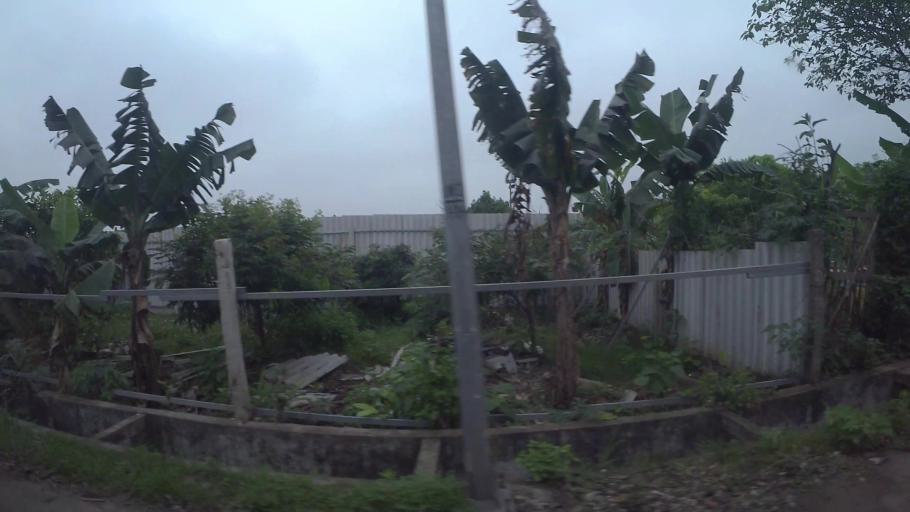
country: VN
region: Hung Yen
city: Van Giang
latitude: 20.9748
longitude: 105.8912
